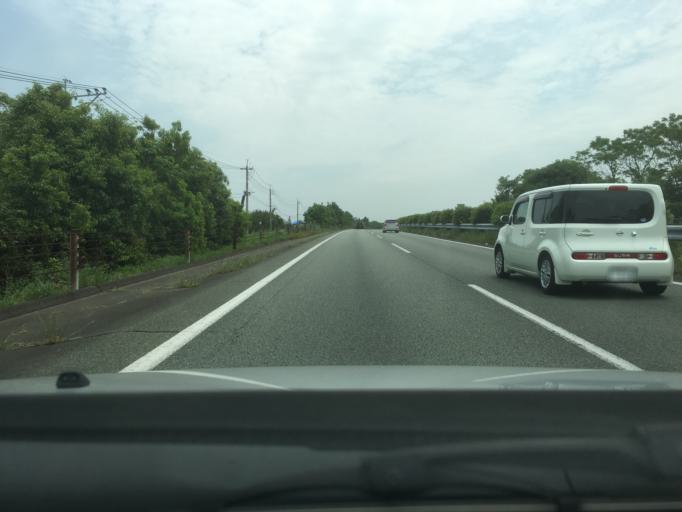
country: JP
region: Kumamoto
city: Kumamoto
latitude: 32.8547
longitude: 130.7584
